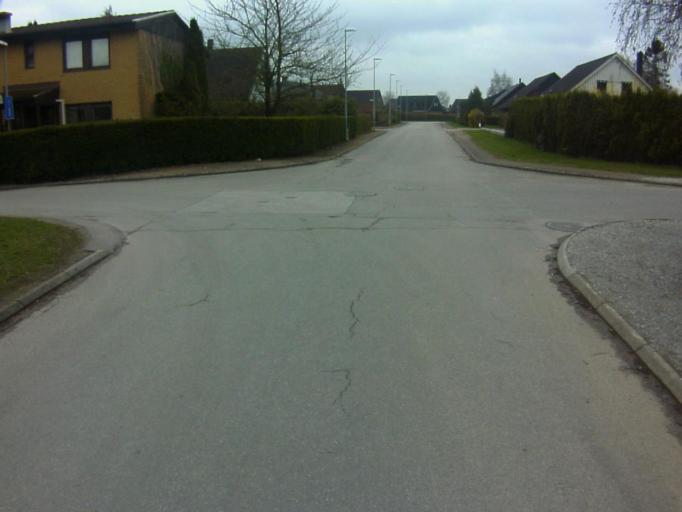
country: SE
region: Skane
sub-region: Kavlinge Kommun
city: Kaevlinge
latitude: 55.7744
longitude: 13.1029
